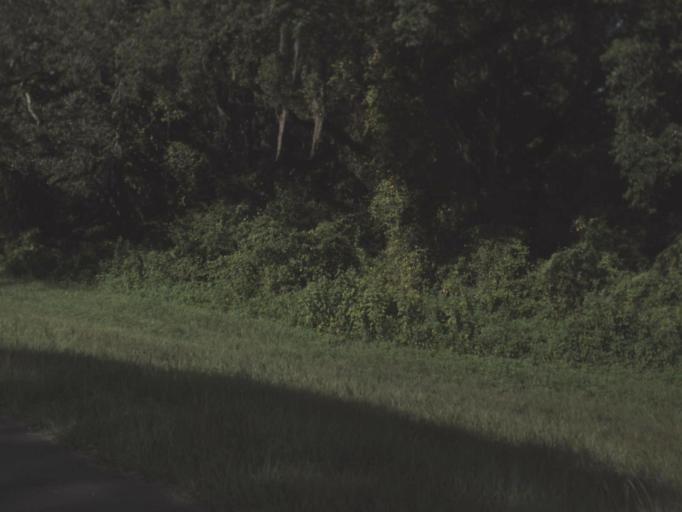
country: US
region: Florida
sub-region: Pasco County
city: Shady Hills
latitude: 28.3882
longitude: -82.4890
